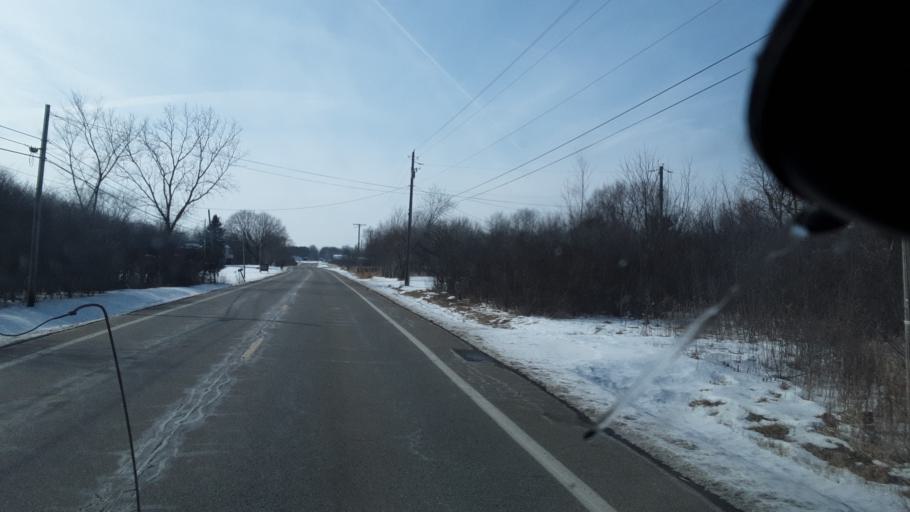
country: US
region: Ohio
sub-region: Mahoning County
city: Craig Beach
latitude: 41.0244
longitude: -80.9764
